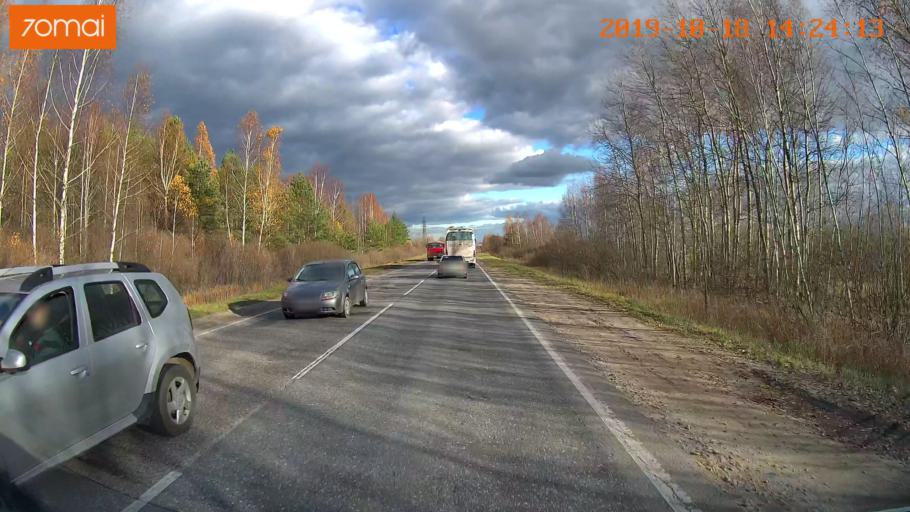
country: RU
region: Rjazan
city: Tuma
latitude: 55.1474
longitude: 40.4961
